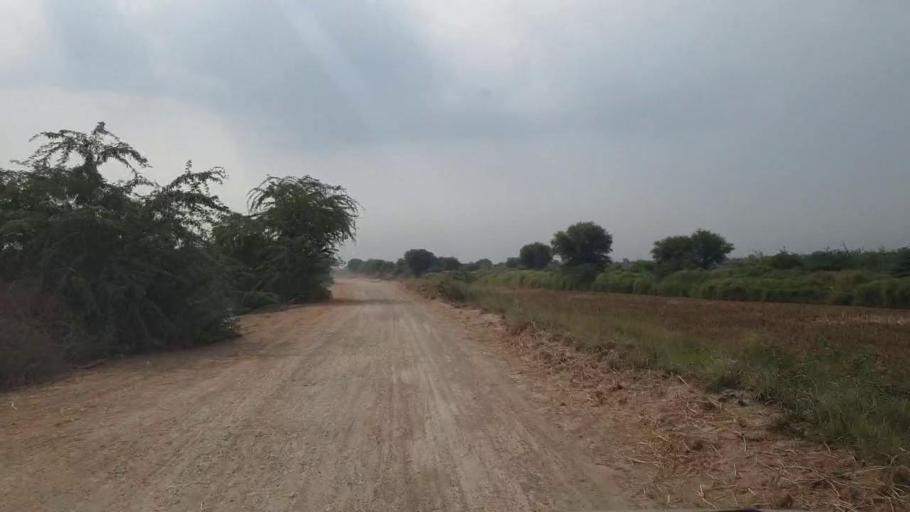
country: PK
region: Sindh
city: Talhar
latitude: 24.9308
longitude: 68.7876
